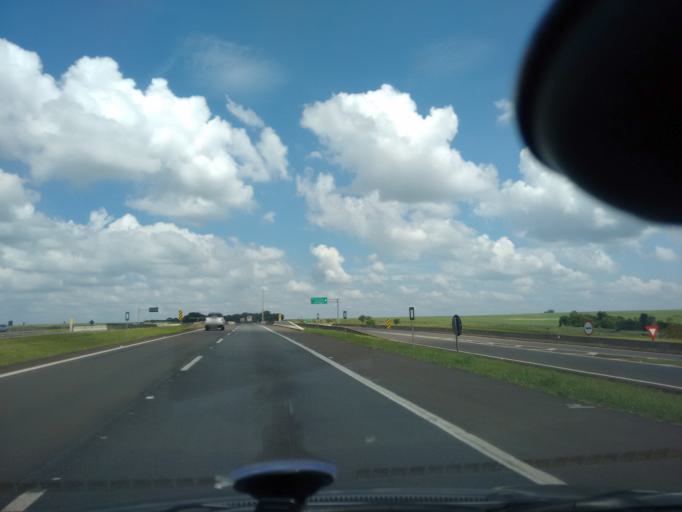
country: BR
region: Sao Paulo
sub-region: Santa Barbara D'Oeste
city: Santa Barbara d'Oeste
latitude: -22.7635
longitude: -47.4457
